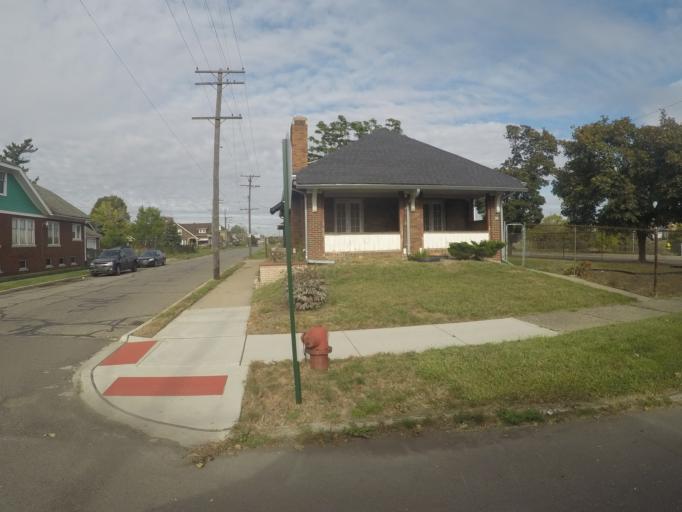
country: US
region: Michigan
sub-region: Wayne County
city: Highland Park
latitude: 42.3647
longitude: -83.1337
